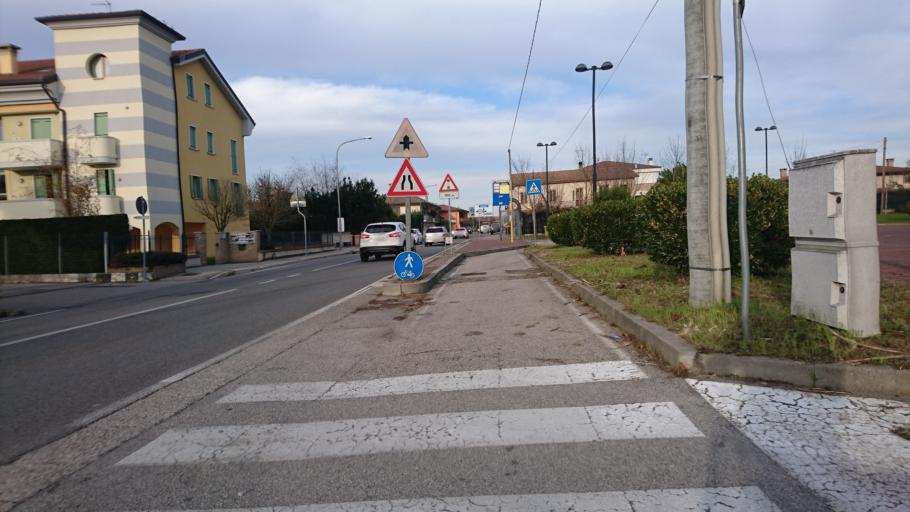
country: IT
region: Veneto
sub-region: Provincia di Padova
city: Polverara
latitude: 45.3147
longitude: 11.9615
